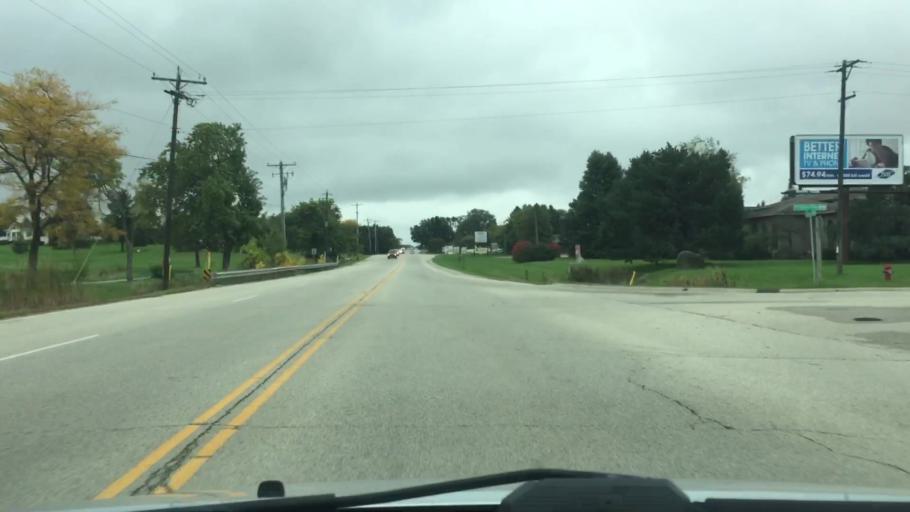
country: US
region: Wisconsin
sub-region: Walworth County
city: Elkhorn
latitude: 42.7174
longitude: -88.5425
